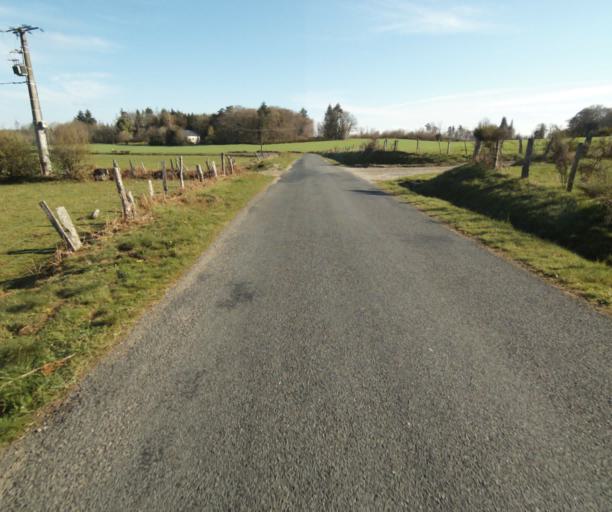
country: FR
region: Limousin
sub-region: Departement de la Correze
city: Correze
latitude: 45.2994
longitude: 1.8699
